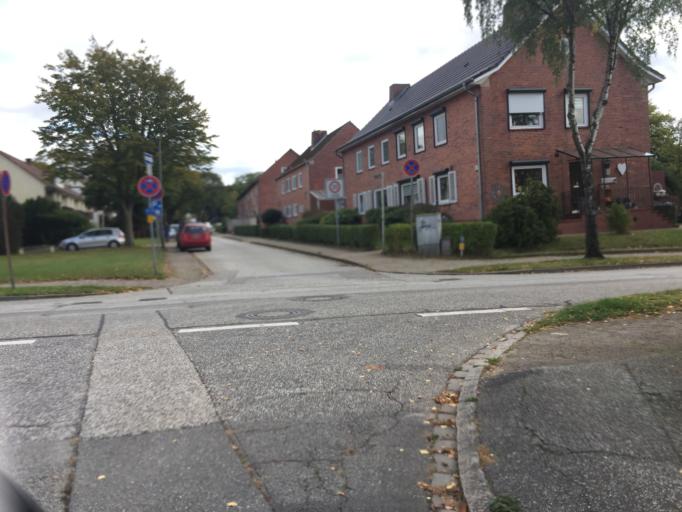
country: DE
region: Schleswig-Holstein
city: Itzehoe
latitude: 53.9398
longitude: 9.5062
